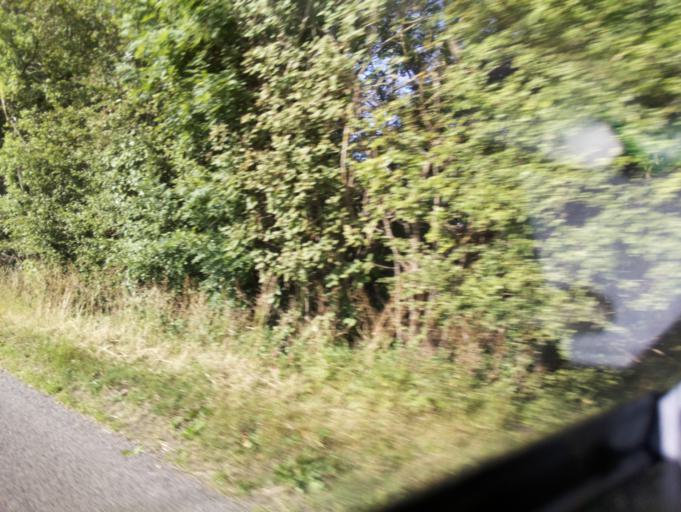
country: GB
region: England
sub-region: Oxfordshire
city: Faringdon
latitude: 51.6698
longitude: -1.5865
